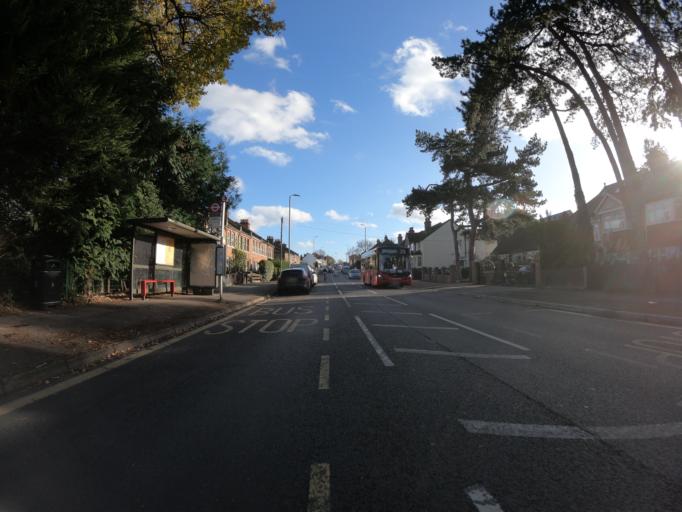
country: GB
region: England
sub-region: Greater London
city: Chislehurst
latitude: 51.4246
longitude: 0.0586
